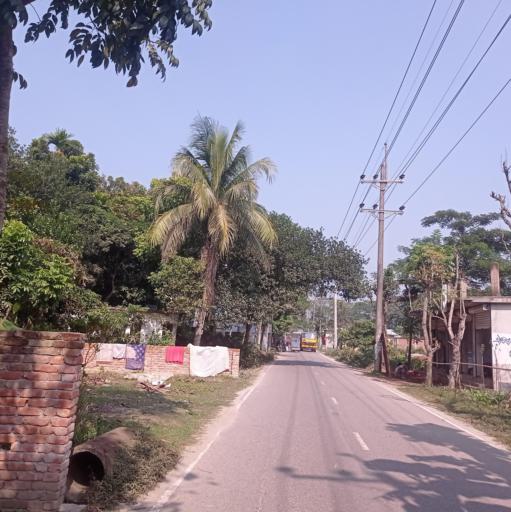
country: BD
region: Dhaka
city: Narsingdi
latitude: 24.0447
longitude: 90.6797
